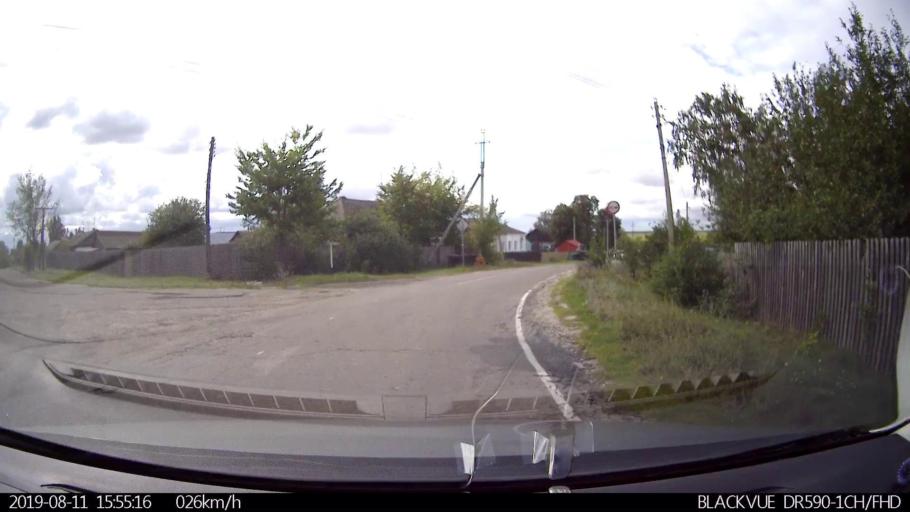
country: RU
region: Ulyanovsk
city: Ignatovka
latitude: 53.9448
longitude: 47.6550
